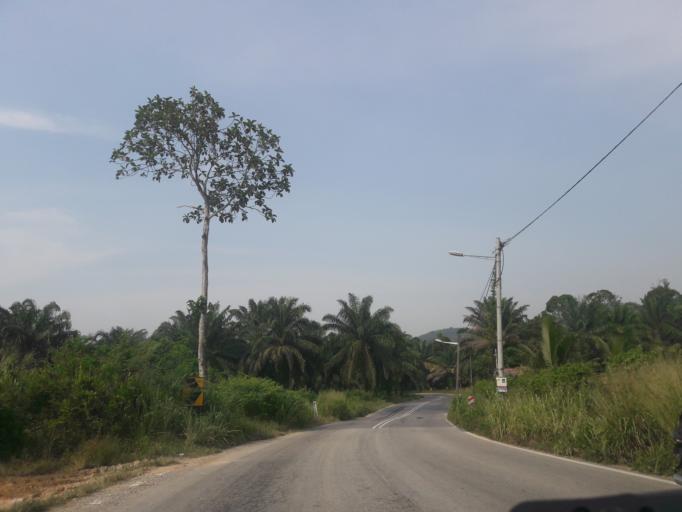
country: MY
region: Kedah
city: Kulim
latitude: 5.3628
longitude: 100.5221
